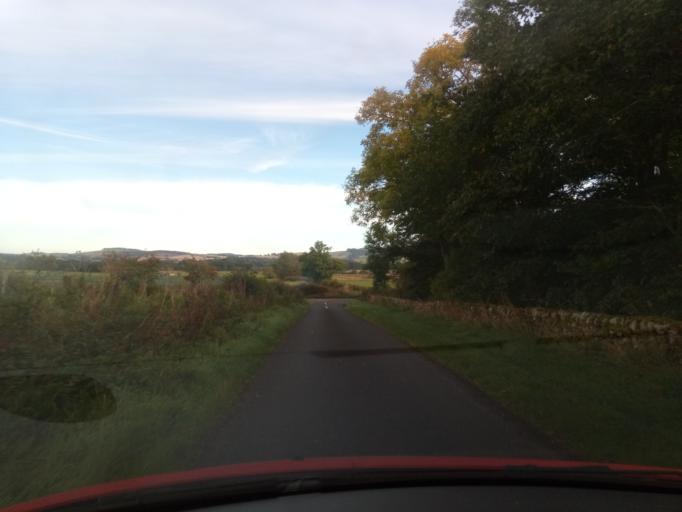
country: GB
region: Scotland
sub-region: The Scottish Borders
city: Kelso
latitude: 55.5169
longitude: -2.3883
